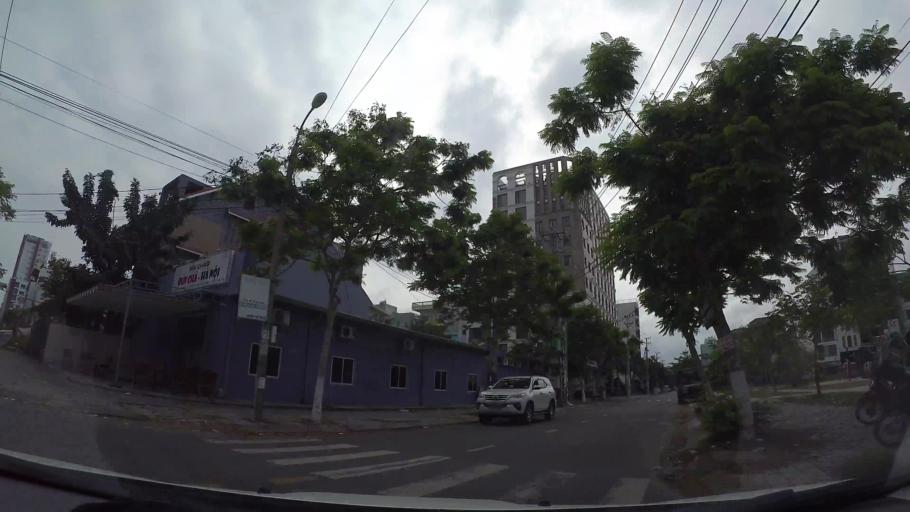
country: VN
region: Da Nang
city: Son Tra
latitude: 16.0755
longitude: 108.2428
